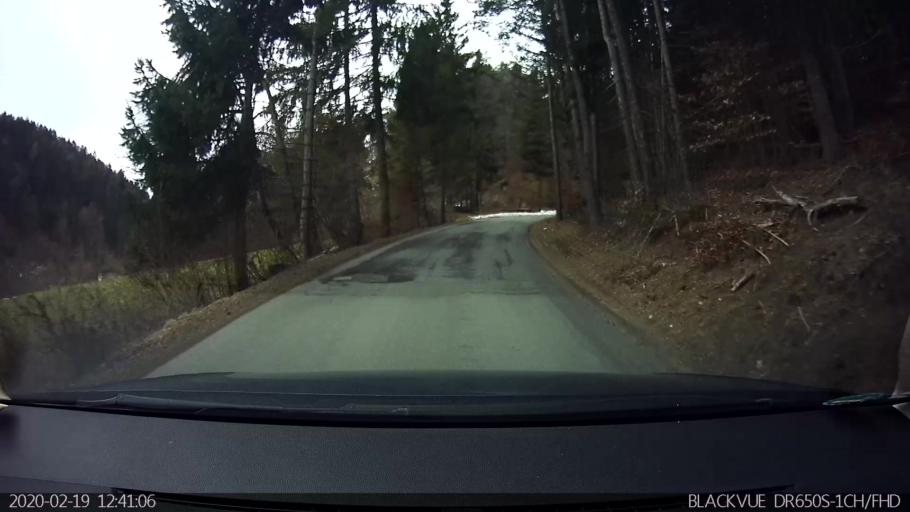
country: AT
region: Tyrol
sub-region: Politischer Bezirk Schwaz
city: Terfens
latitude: 47.3280
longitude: 11.6321
